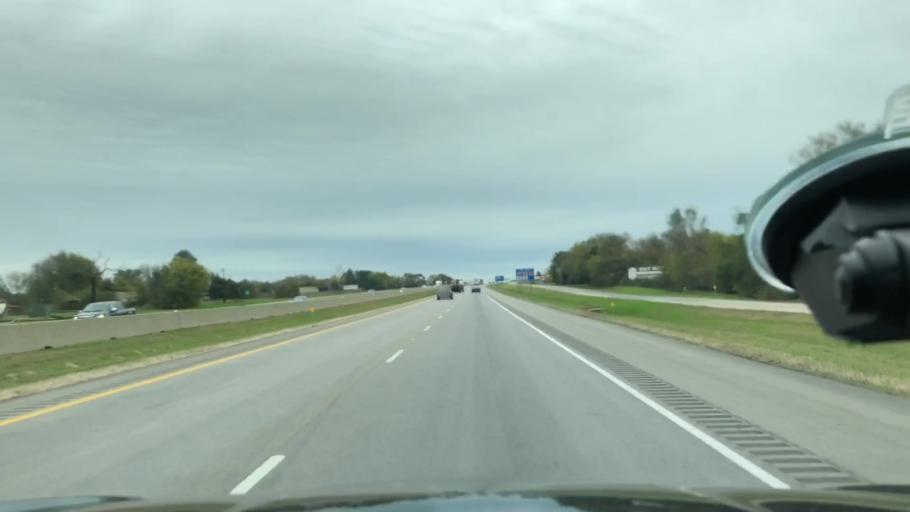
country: US
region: Texas
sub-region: Franklin County
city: Mount Vernon
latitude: 33.1631
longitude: -95.2558
